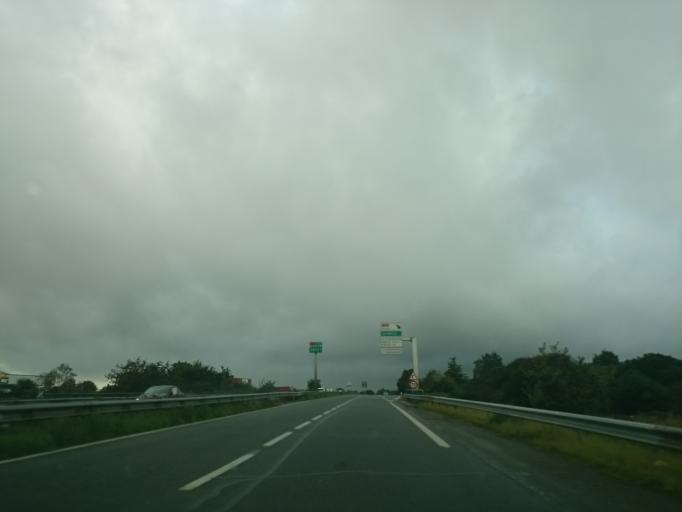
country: FR
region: Brittany
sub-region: Departement du Finistere
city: Gouesnou
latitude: 48.4339
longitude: -4.4421
